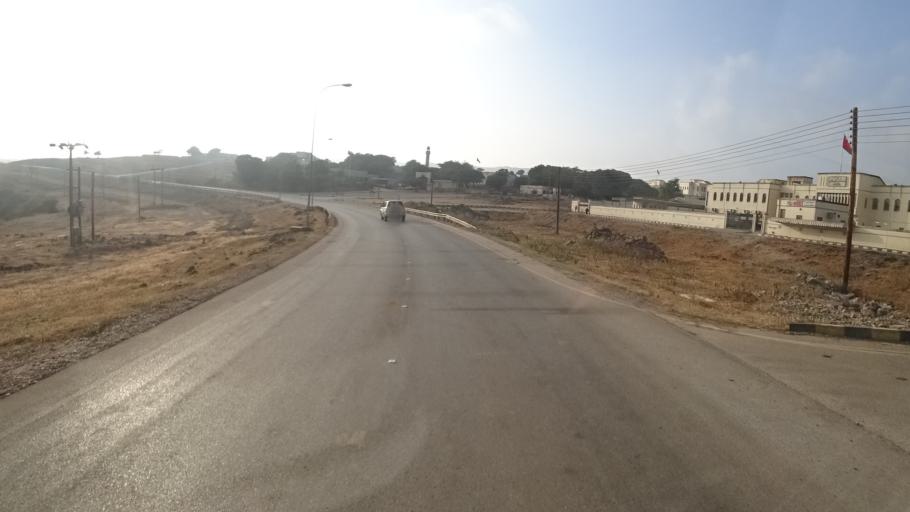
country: OM
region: Zufar
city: Salalah
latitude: 17.1255
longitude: 53.9974
